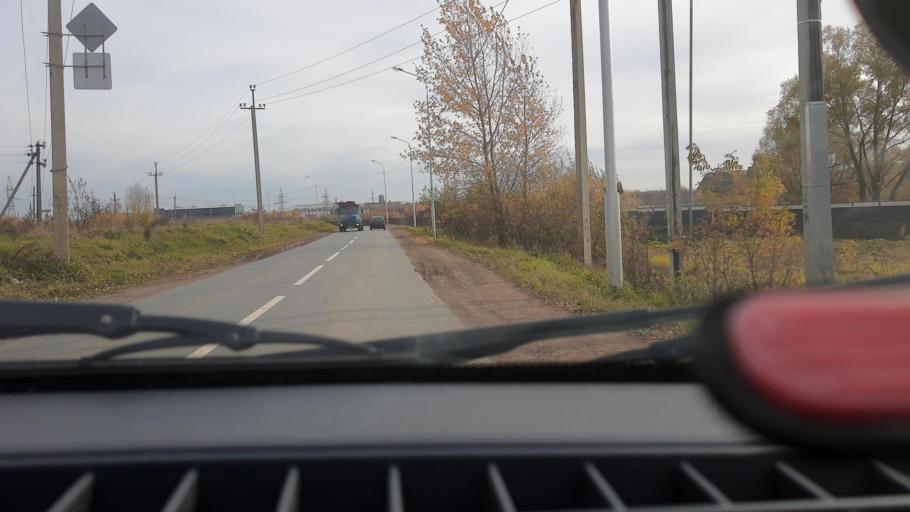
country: RU
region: Bashkortostan
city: Ufa
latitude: 54.6666
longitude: 55.9175
